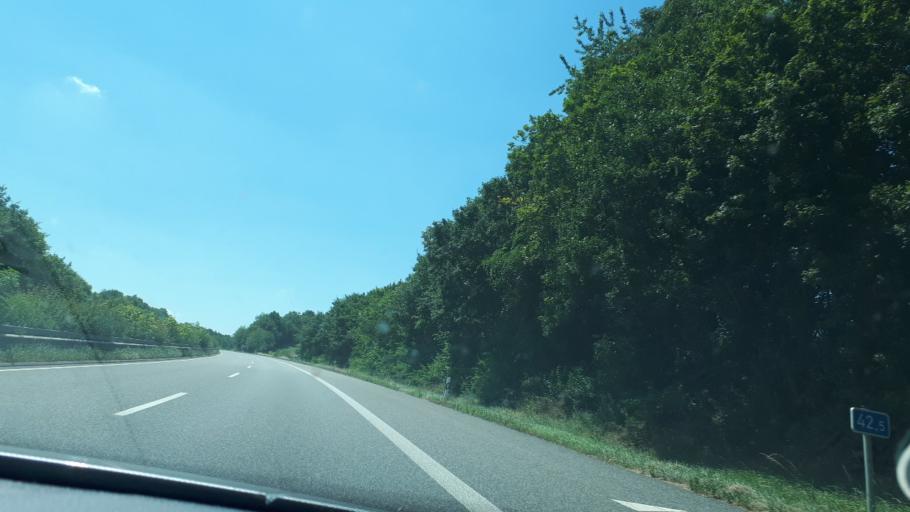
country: DE
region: Rheinland-Pfalz
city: Trimbs
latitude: 50.3101
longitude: 7.2923
